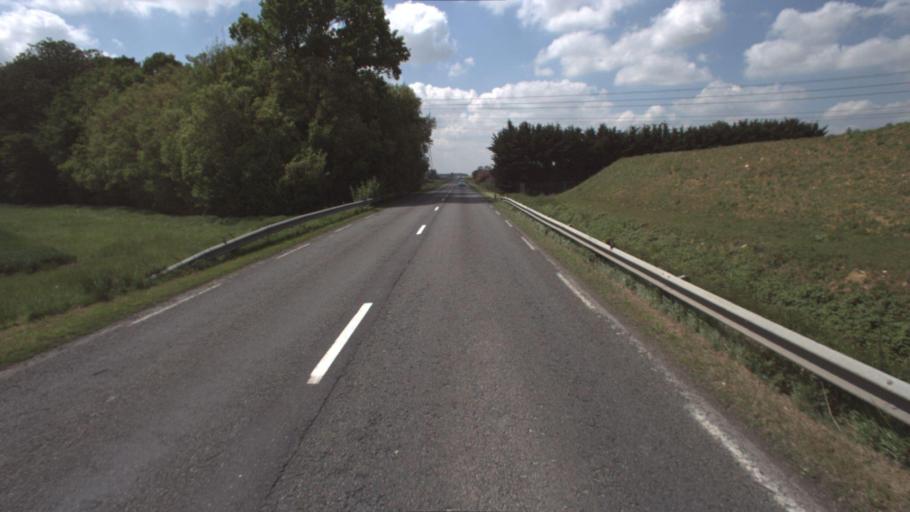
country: FR
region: Ile-de-France
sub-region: Departement de Seine-et-Marne
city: Moisenay
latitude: 48.6109
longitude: 2.7447
